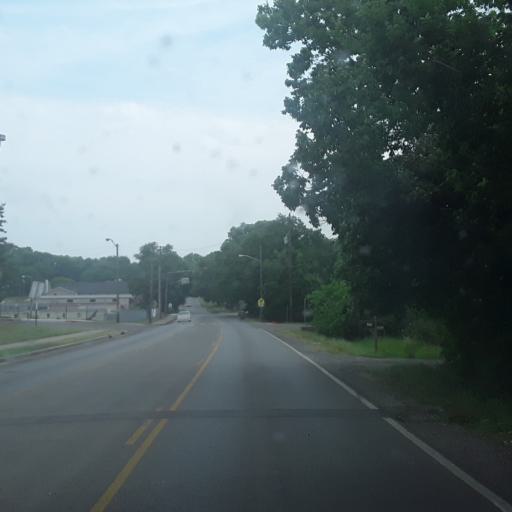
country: US
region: Tennessee
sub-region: Williamson County
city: Brentwood
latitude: 36.0567
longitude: -86.7227
